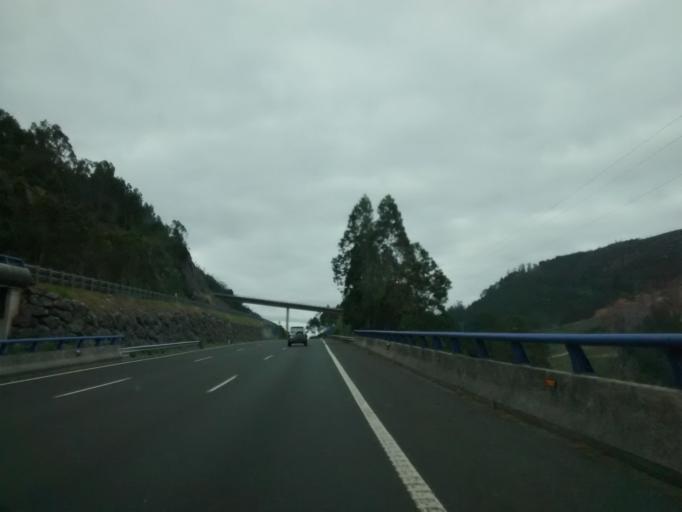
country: ES
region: Cantabria
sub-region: Provincia de Cantabria
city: Los Corrales de Buelna
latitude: 43.2920
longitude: -4.0782
